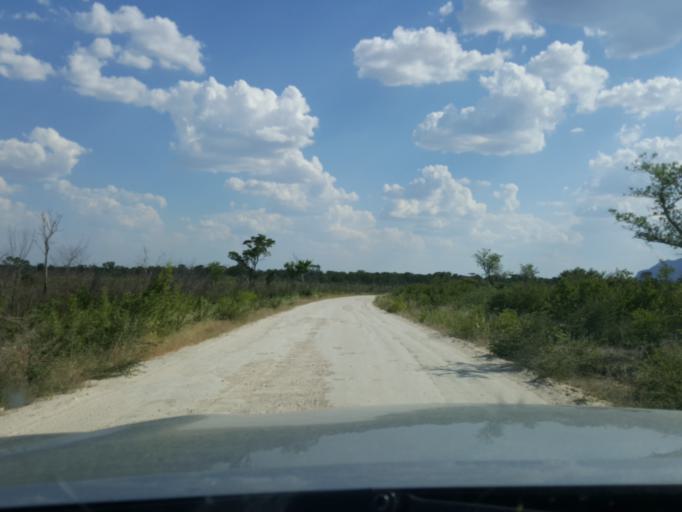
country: BW
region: North West
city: Shakawe
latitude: -18.7326
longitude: 21.8317
